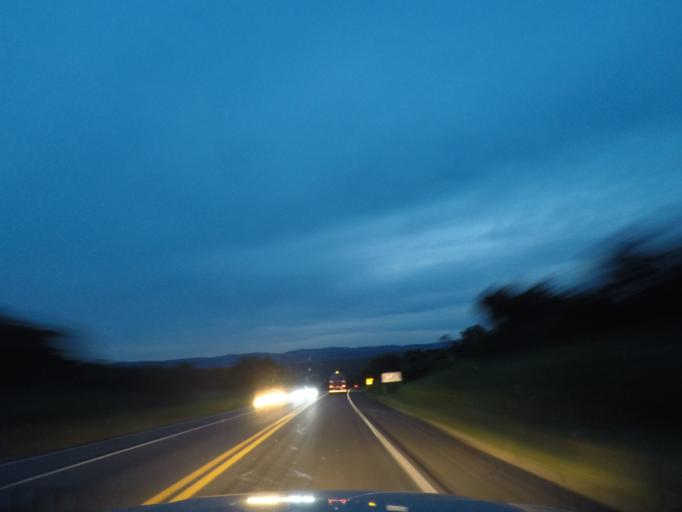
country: BR
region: Bahia
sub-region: Andarai
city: Vera Cruz
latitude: -12.4955
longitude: -41.3177
